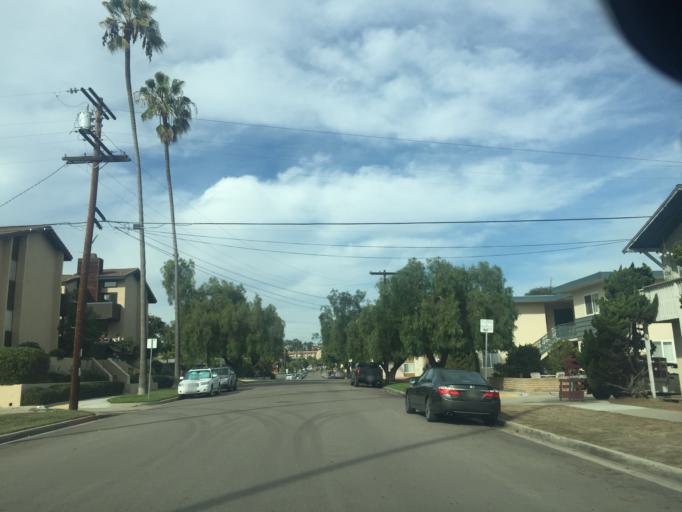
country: US
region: California
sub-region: San Diego County
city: La Jolla
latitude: 32.7971
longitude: -117.2361
